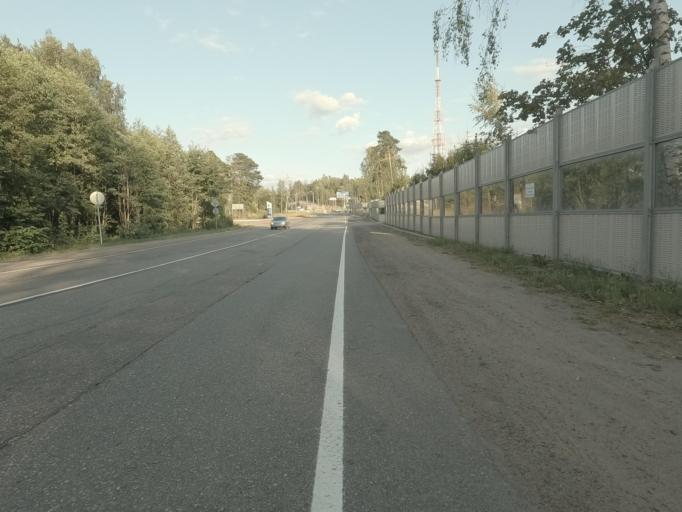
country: RU
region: Leningrad
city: Vyborg
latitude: 60.7250
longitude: 28.7640
